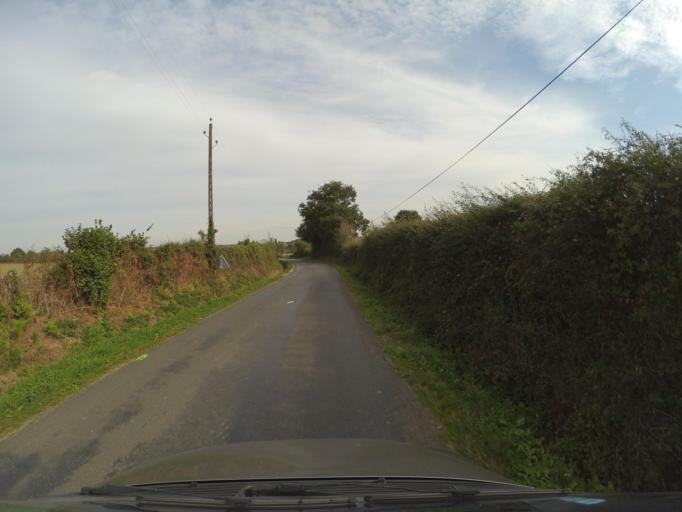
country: FR
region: Pays de la Loire
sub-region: Departement de Maine-et-Loire
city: La Jubaudiere
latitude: 47.1862
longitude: -0.9120
